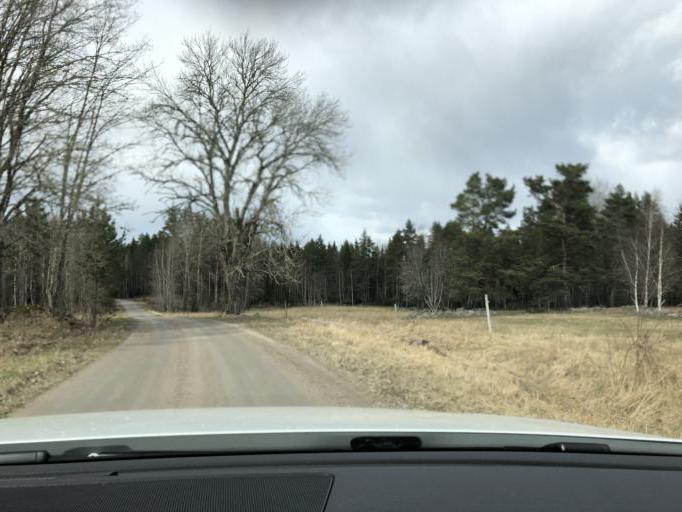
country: SE
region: Gaevleborg
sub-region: Gavle Kommun
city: Hedesunda
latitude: 60.3171
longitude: 17.1060
